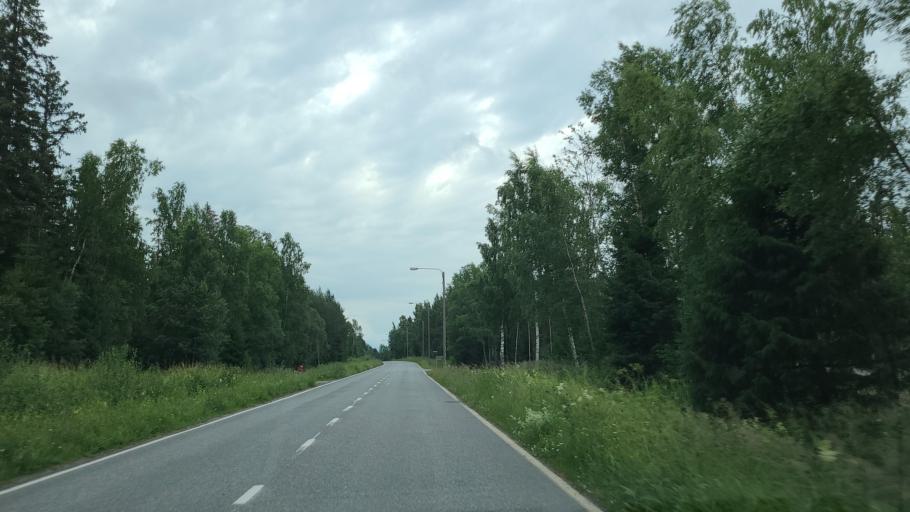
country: FI
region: Ostrobothnia
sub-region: Vaasa
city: Replot
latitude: 63.2363
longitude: 21.3969
